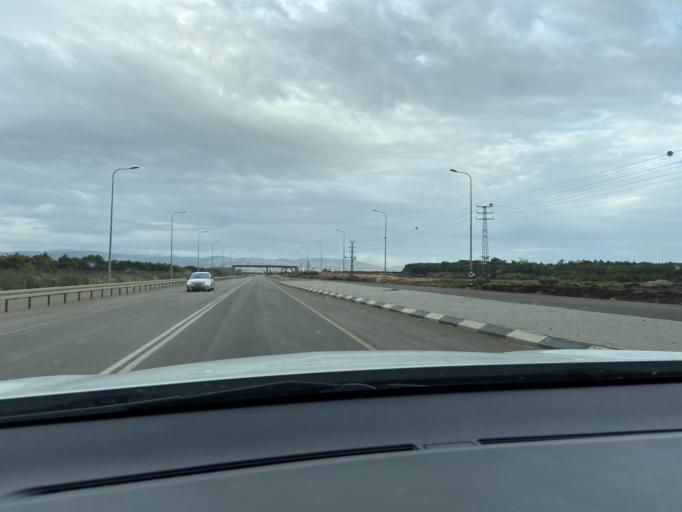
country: IL
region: Northern District
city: El Mazra`a
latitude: 32.9788
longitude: 35.1096
